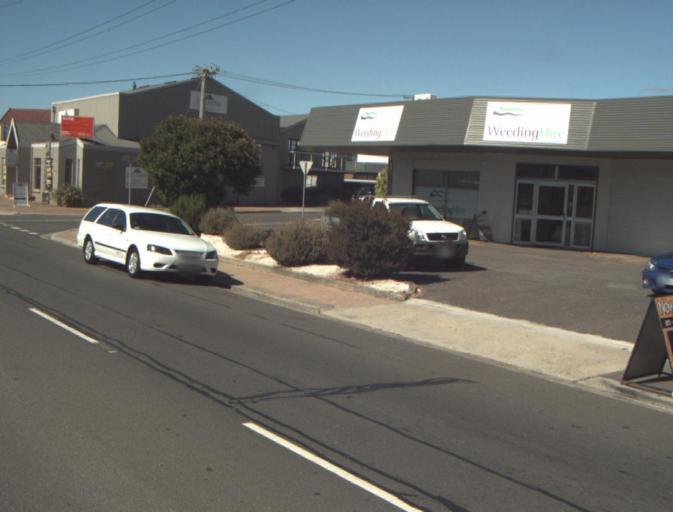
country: AU
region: Tasmania
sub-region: Launceston
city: Newnham
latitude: -41.4117
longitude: 147.1327
